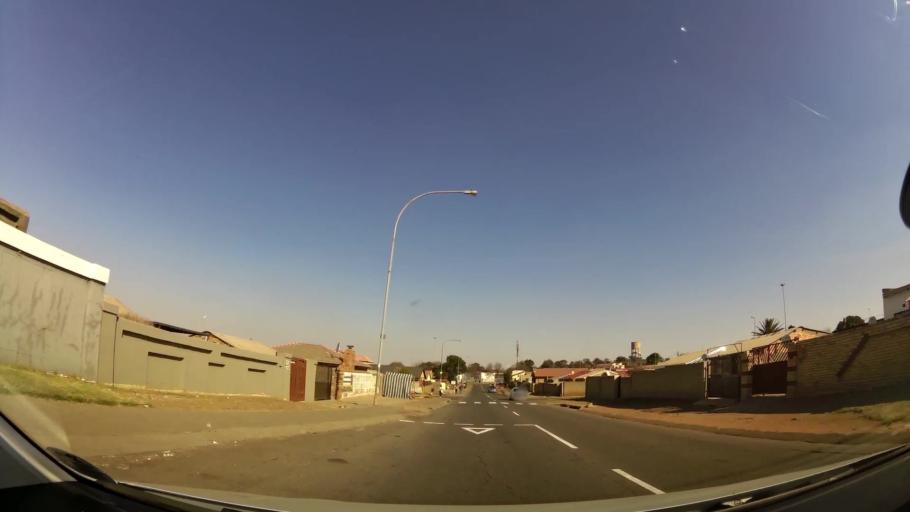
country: ZA
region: Gauteng
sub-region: City of Johannesburg Metropolitan Municipality
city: Soweto
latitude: -26.2773
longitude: 27.8709
